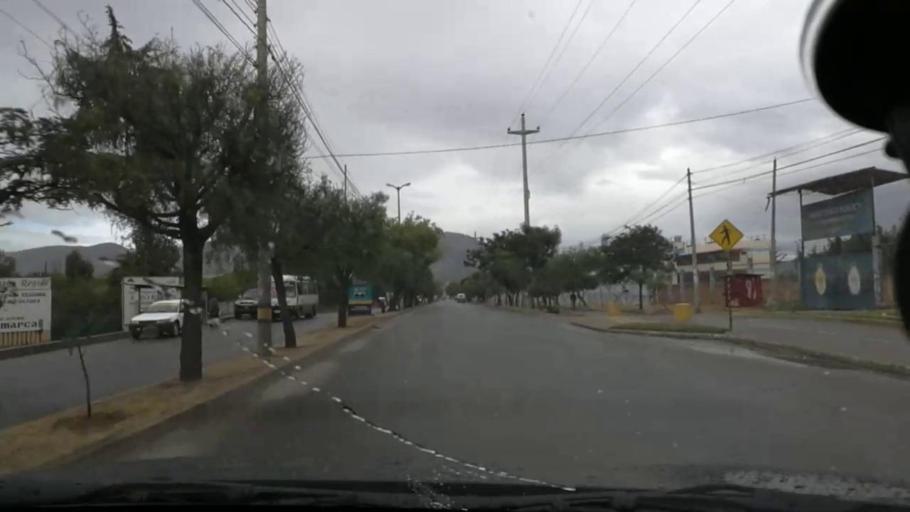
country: PE
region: Cajamarca
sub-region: Provincia de Cajamarca
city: Cajamarca
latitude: -7.1654
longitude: -78.4925
